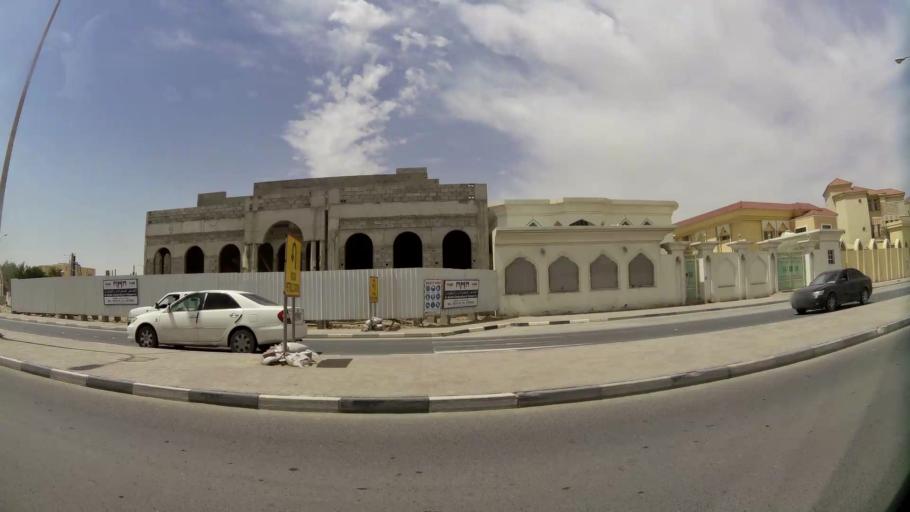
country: QA
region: Baladiyat ar Rayyan
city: Ar Rayyan
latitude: 25.3005
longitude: 51.4121
